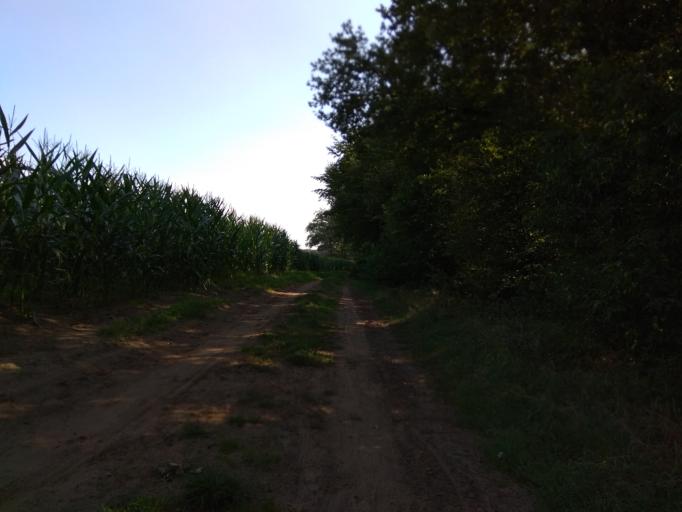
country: DE
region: North Rhine-Westphalia
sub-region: Regierungsbezirk Munster
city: Klein Reken
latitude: 51.7474
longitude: 7.0359
